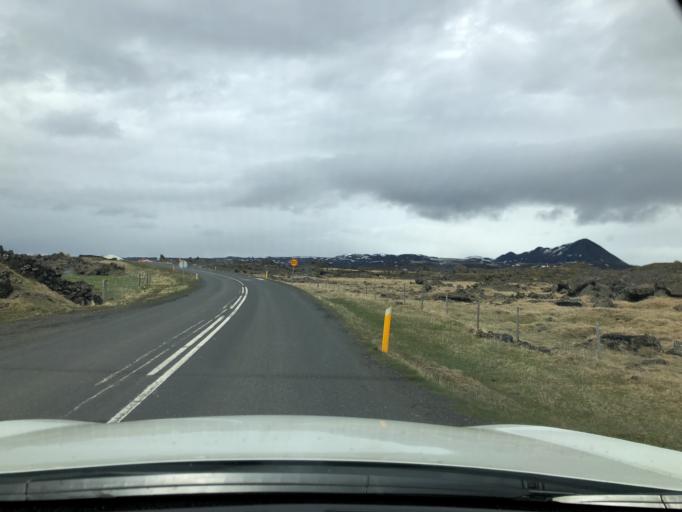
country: IS
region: Northeast
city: Laugar
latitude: 65.6163
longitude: -16.9159
